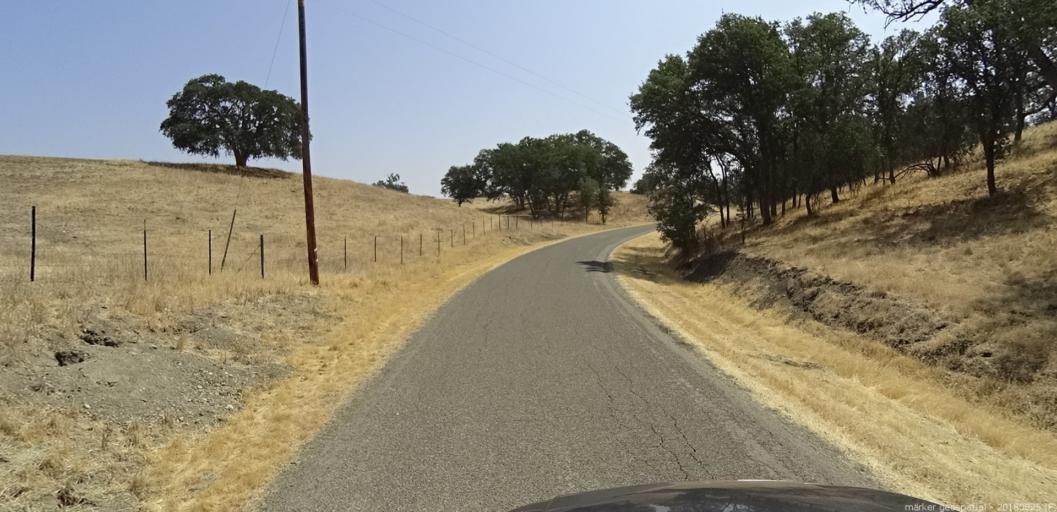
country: US
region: California
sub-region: San Luis Obispo County
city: Shandon
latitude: 35.8784
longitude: -120.4100
